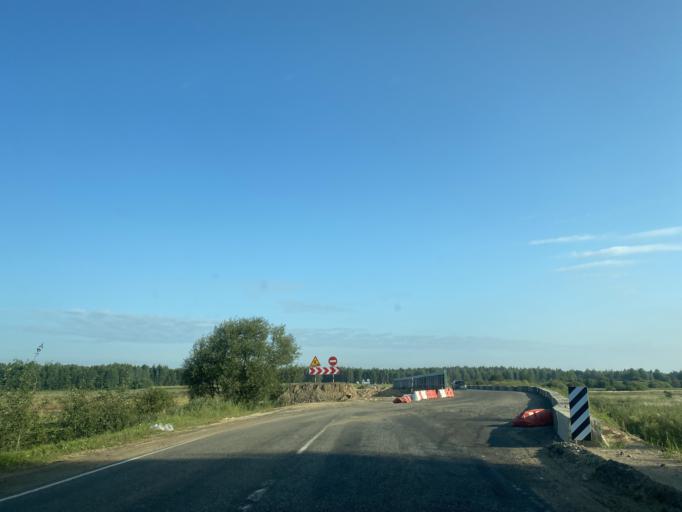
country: BY
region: Minsk
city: Loshnitsa
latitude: 54.0951
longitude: 28.6938
